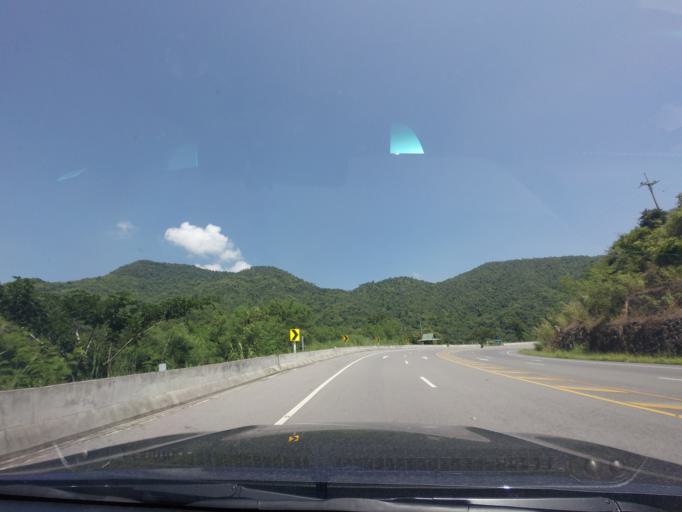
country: TH
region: Phetchabun
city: Lom Sak
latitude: 16.7731
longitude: 101.1301
